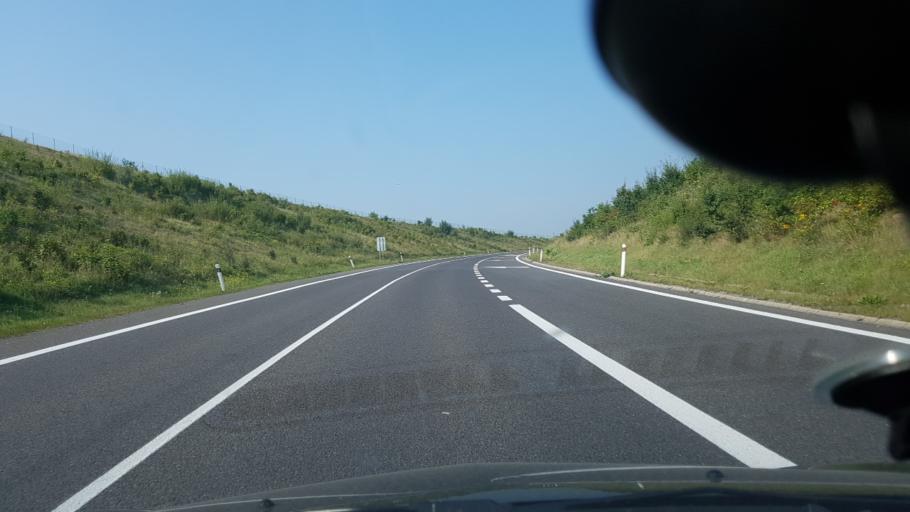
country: SK
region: Zilinsky
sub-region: Okres Zilina
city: Trstena
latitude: 49.3602
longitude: 19.6326
